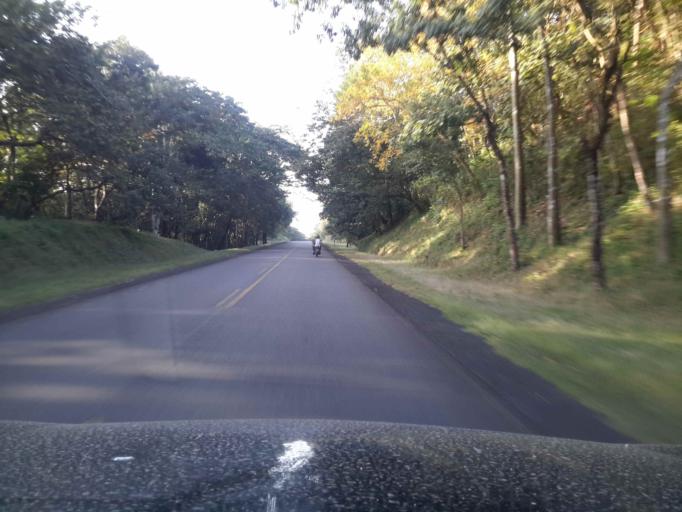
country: NI
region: Rio San Juan
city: San Miguelito
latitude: 11.4070
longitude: -84.8337
